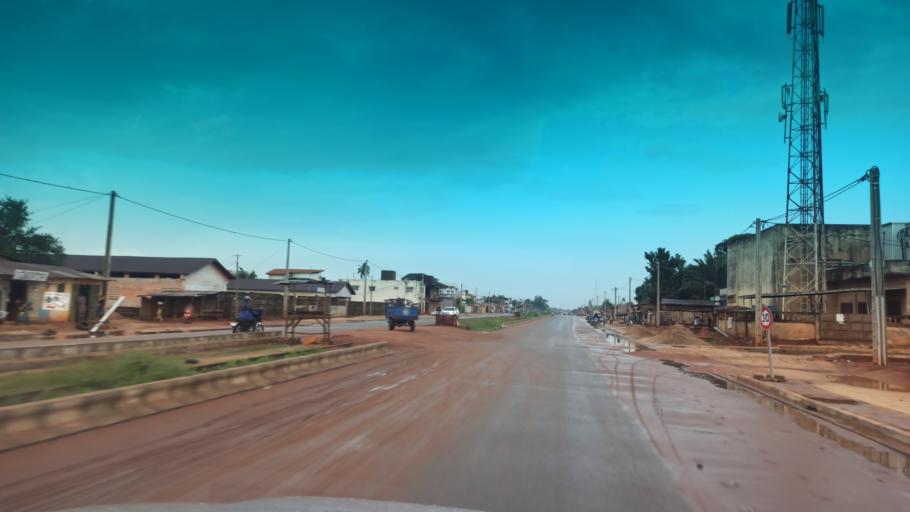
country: BJ
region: Queme
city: Porto-Novo
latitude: 6.4946
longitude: 2.6262
